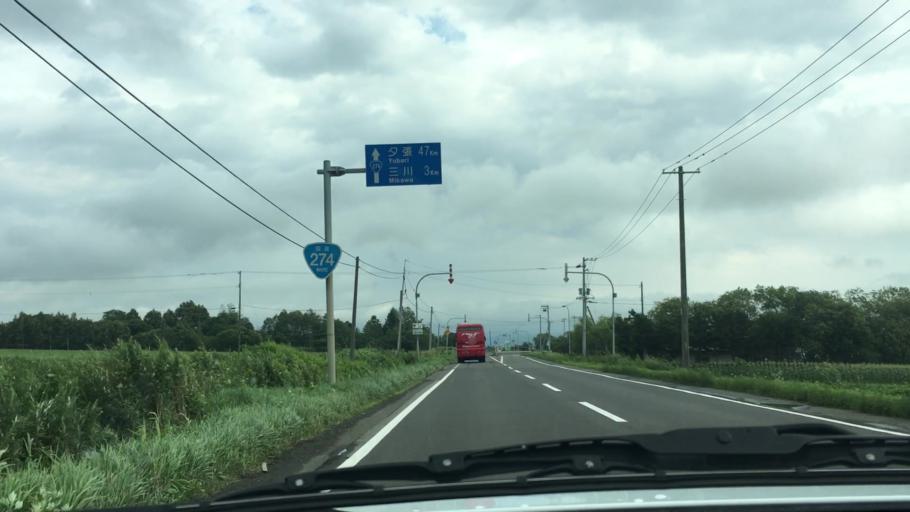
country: JP
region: Hokkaido
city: Chitose
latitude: 42.9448
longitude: 141.7650
